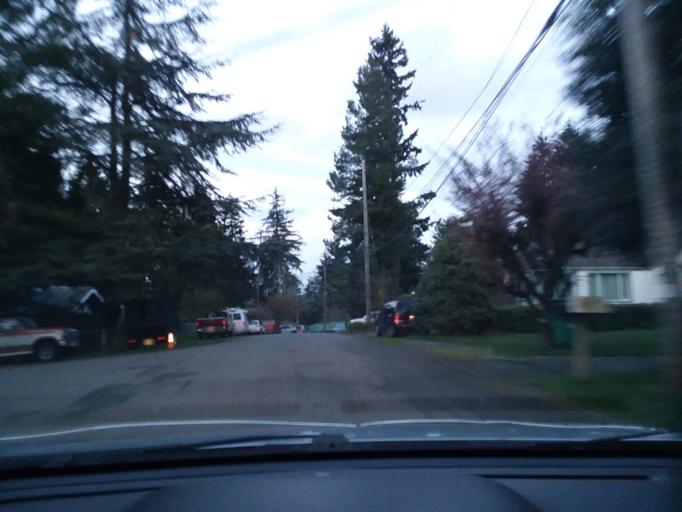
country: US
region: Washington
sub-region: Snohomish County
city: Mountlake Terrace
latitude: 47.7639
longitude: -122.3160
